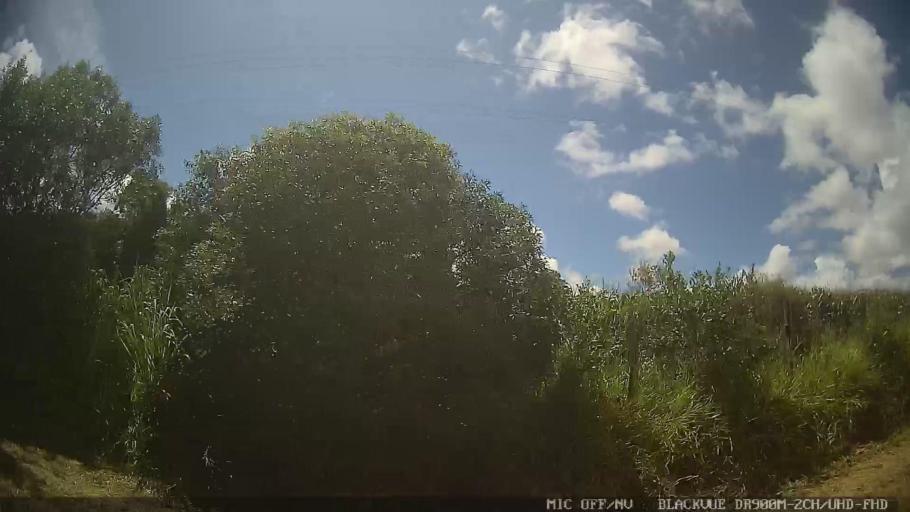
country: BR
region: Sao Paulo
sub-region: Amparo
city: Amparo
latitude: -22.8329
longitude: -46.7034
